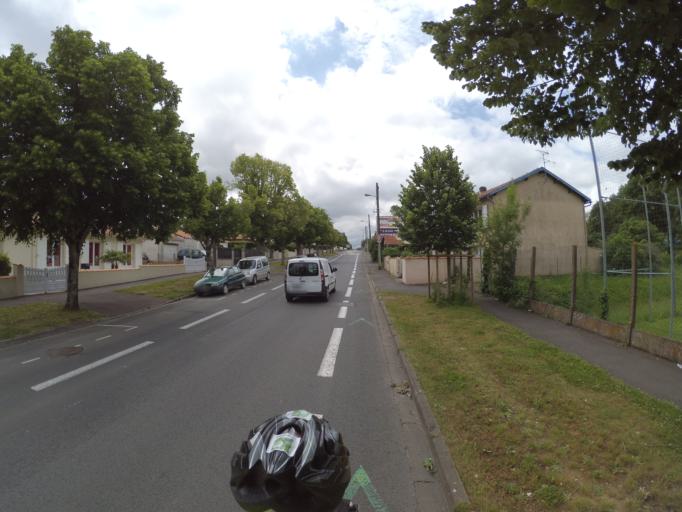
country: FR
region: Poitou-Charentes
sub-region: Departement de la Charente-Maritime
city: Rochefort
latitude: 45.9541
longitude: -0.9690
